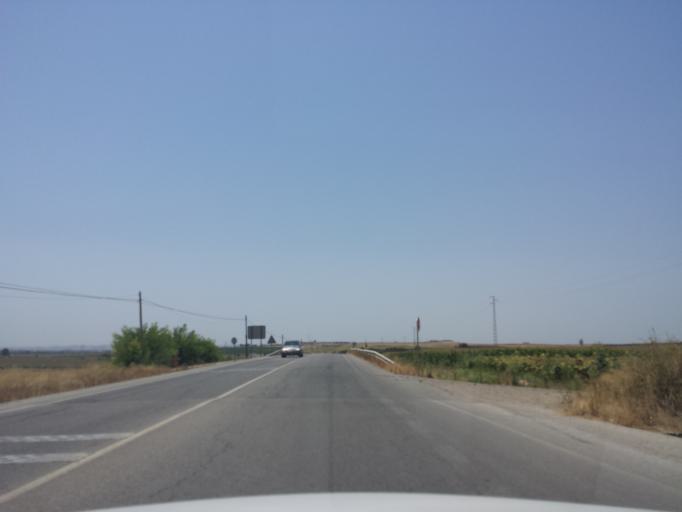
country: ES
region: Andalusia
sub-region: Provincia de Sevilla
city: Acala del Rio
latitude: 37.5420
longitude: -5.9460
